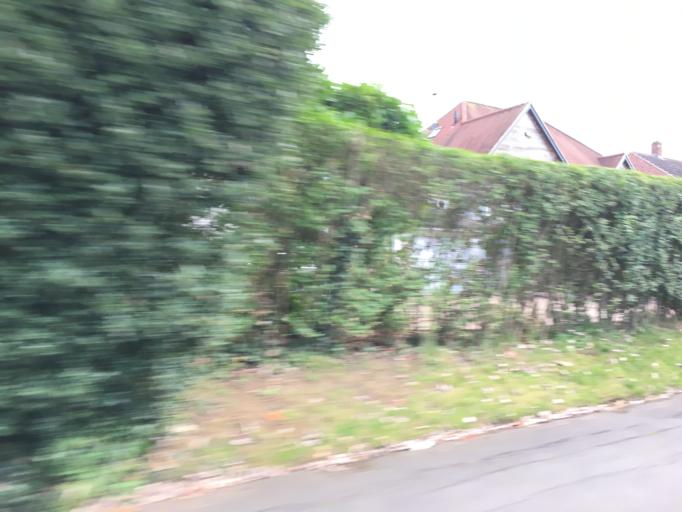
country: GB
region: England
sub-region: Warwickshire
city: Dunchurch
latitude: 52.3557
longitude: -1.2848
